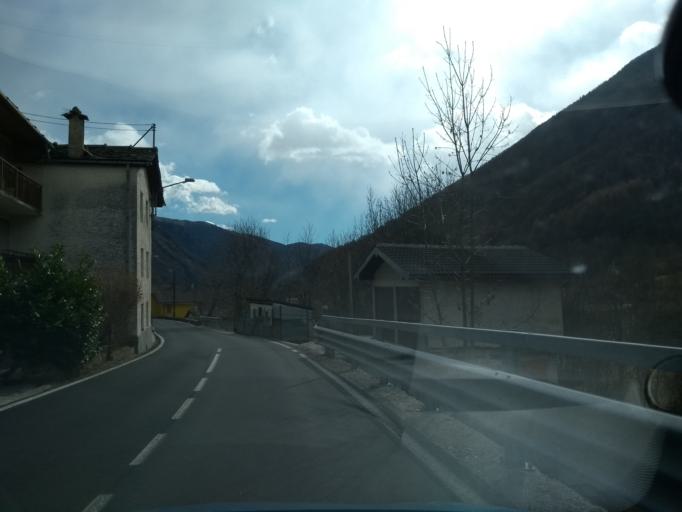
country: IT
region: Piedmont
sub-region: Provincia di Torino
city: Chialamberto
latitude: 45.3652
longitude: 7.3350
